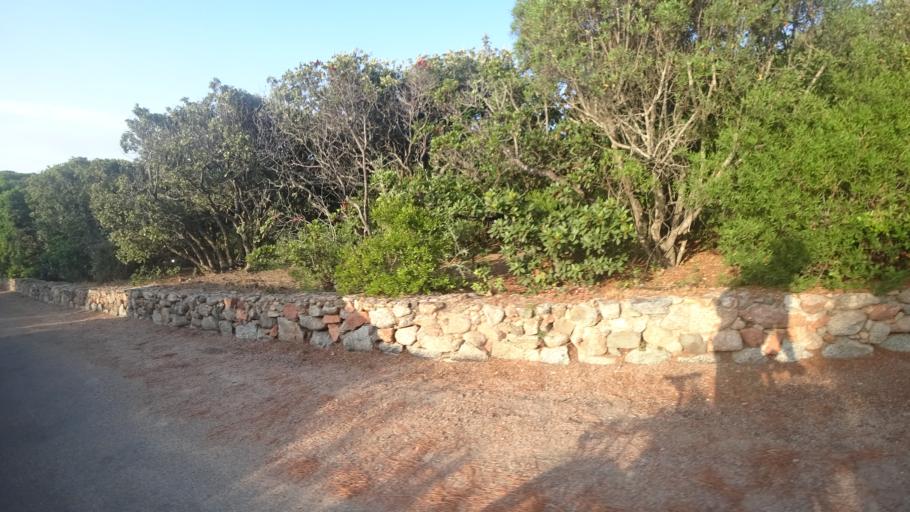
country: FR
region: Corsica
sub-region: Departement de la Corse-du-Sud
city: Porto-Vecchio
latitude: 41.6208
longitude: 9.3531
